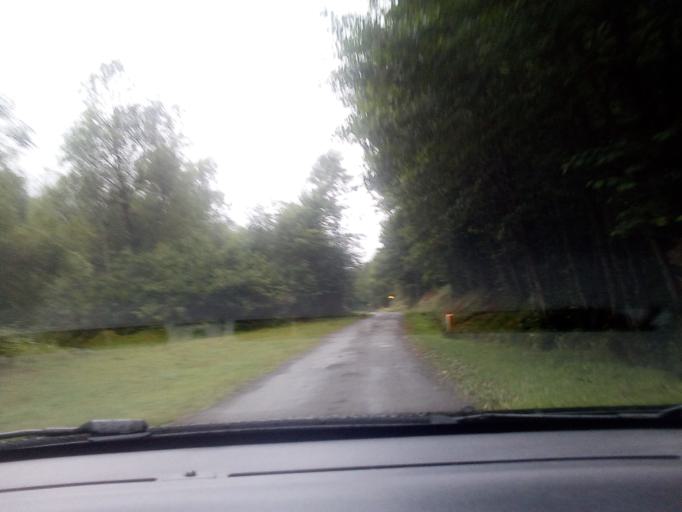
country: FR
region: Midi-Pyrenees
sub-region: Departement des Hautes-Pyrenees
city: Campan
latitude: 42.9426
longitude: 0.2183
